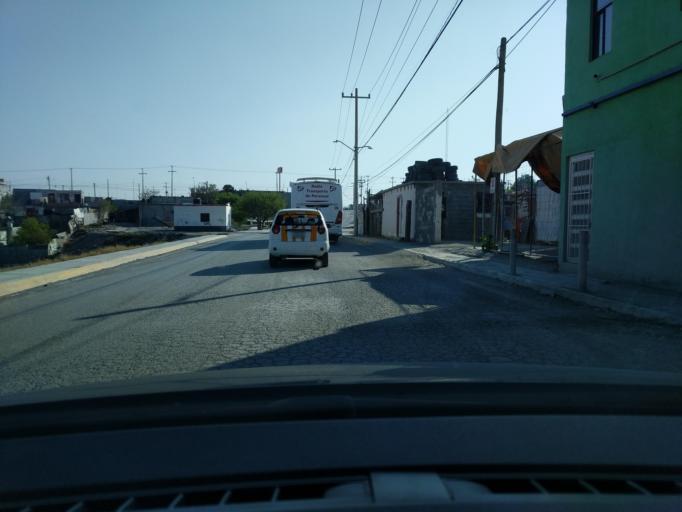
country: MX
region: Coahuila
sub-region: Ramos Arizpe
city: Ramos Arizpe
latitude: 25.5556
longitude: -100.9621
